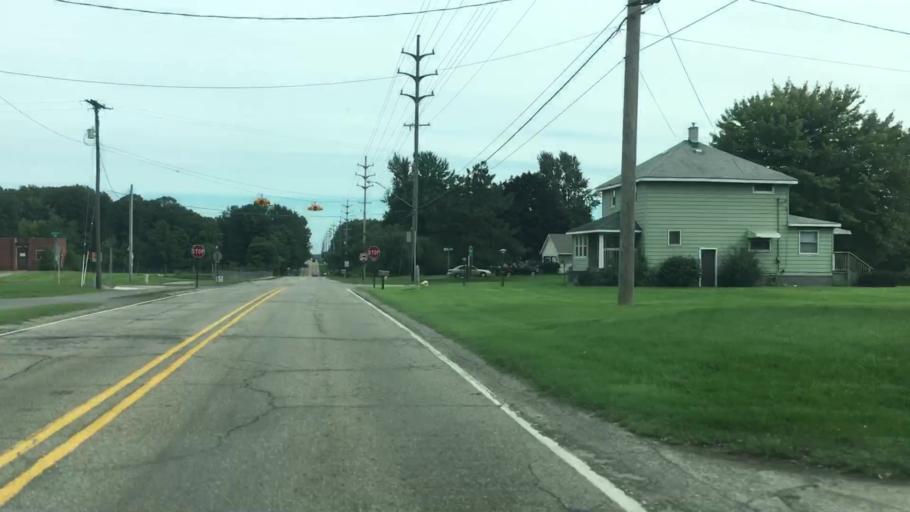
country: US
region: Michigan
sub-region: Ottawa County
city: Jenison
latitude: 42.8629
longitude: -85.7821
